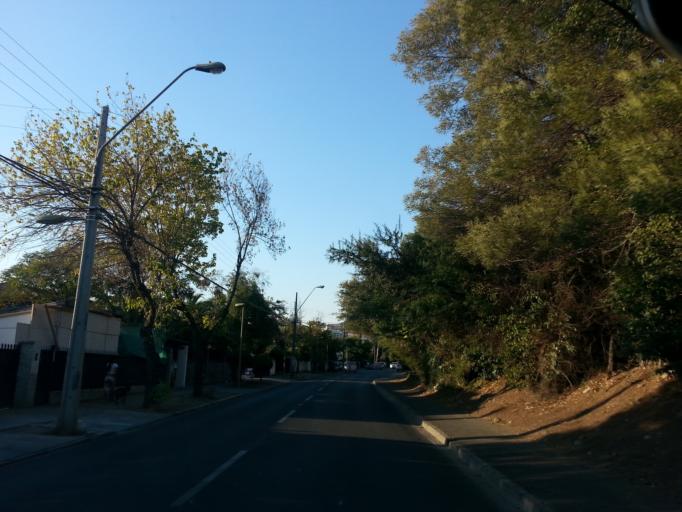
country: CL
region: Santiago Metropolitan
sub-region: Provincia de Santiago
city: Villa Presidente Frei, Nunoa, Santiago, Chile
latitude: -33.3960
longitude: -70.5399
